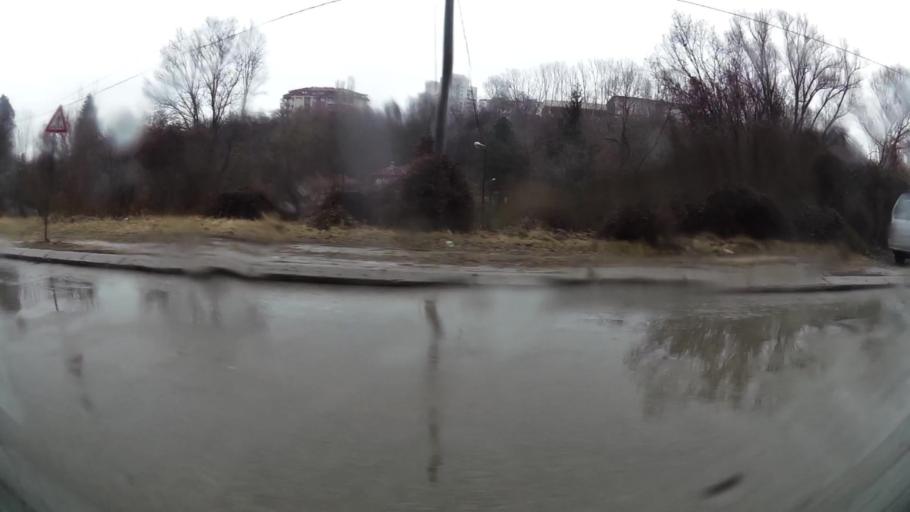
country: BG
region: Sofia-Capital
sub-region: Stolichna Obshtina
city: Sofia
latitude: 42.6524
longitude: 23.3655
